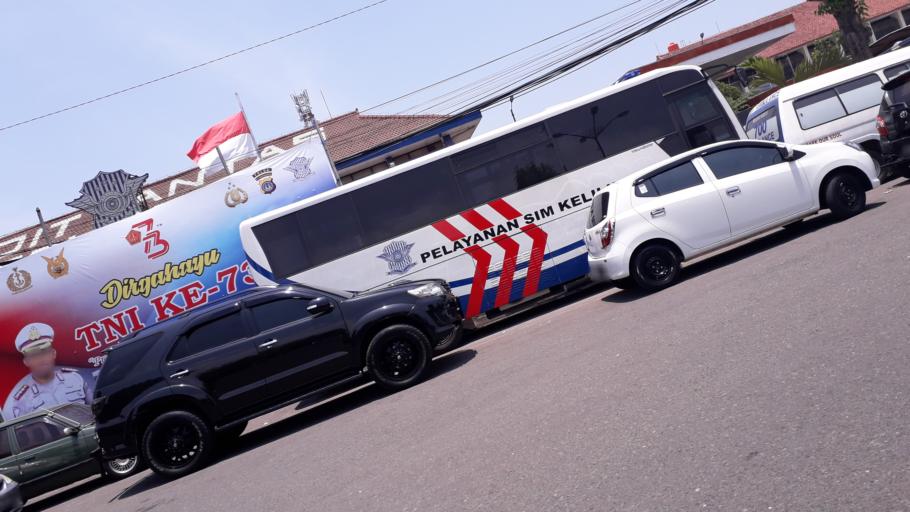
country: ID
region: Daerah Istimewa Yogyakarta
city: Yogyakarta
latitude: -7.7876
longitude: 110.3596
